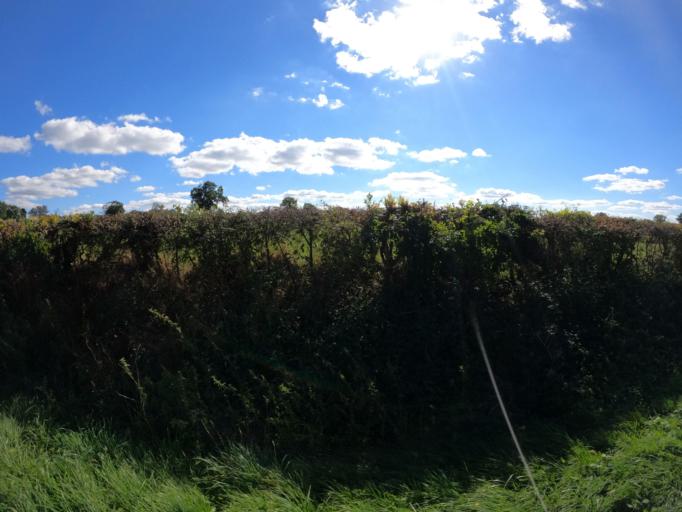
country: FR
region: Auvergne
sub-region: Departement de l'Allier
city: Buxieres-les-Mines
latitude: 46.4031
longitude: 2.9345
